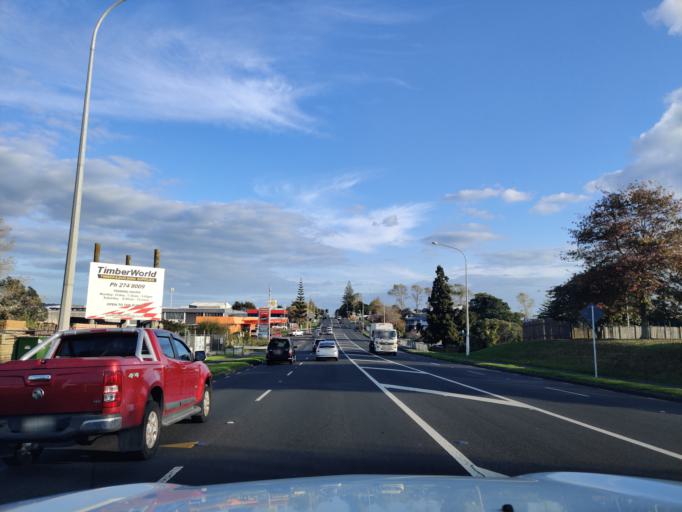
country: NZ
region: Auckland
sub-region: Auckland
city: Manukau City
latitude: -36.9549
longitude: 174.8906
